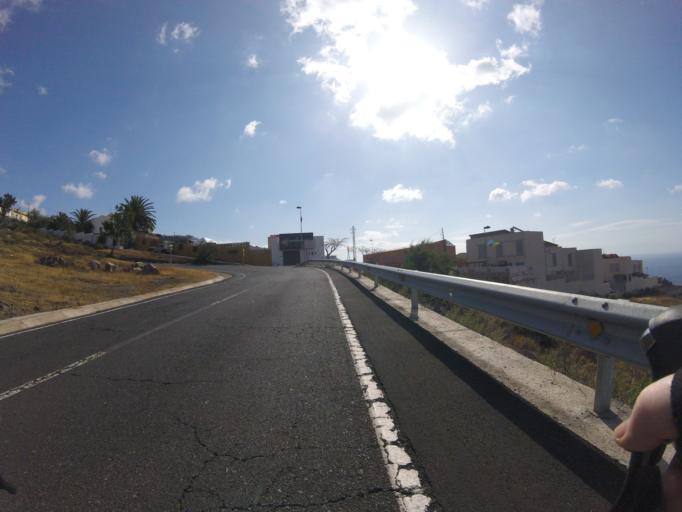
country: ES
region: Canary Islands
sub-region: Provincia de Santa Cruz de Tenerife
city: La Laguna
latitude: 28.4133
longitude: -16.3234
